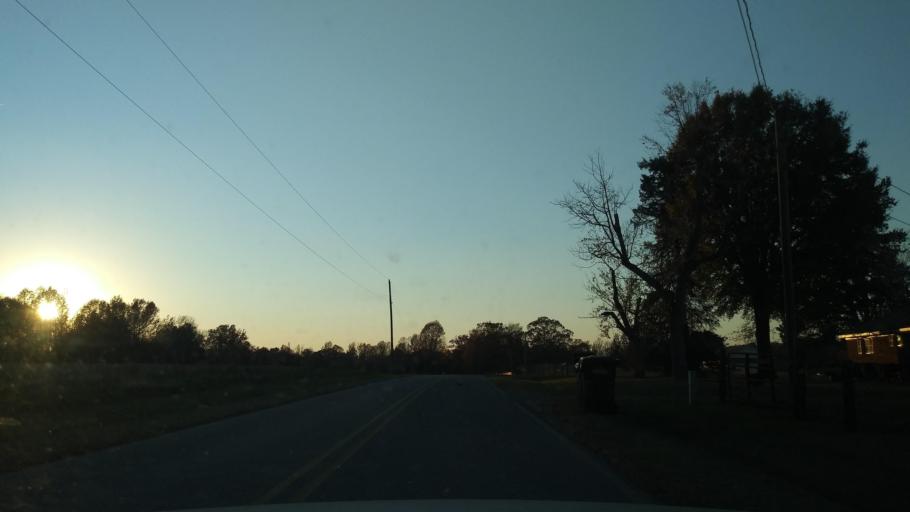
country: US
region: North Carolina
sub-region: Guilford County
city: Pleasant Garden
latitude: 36.0009
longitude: -79.7735
